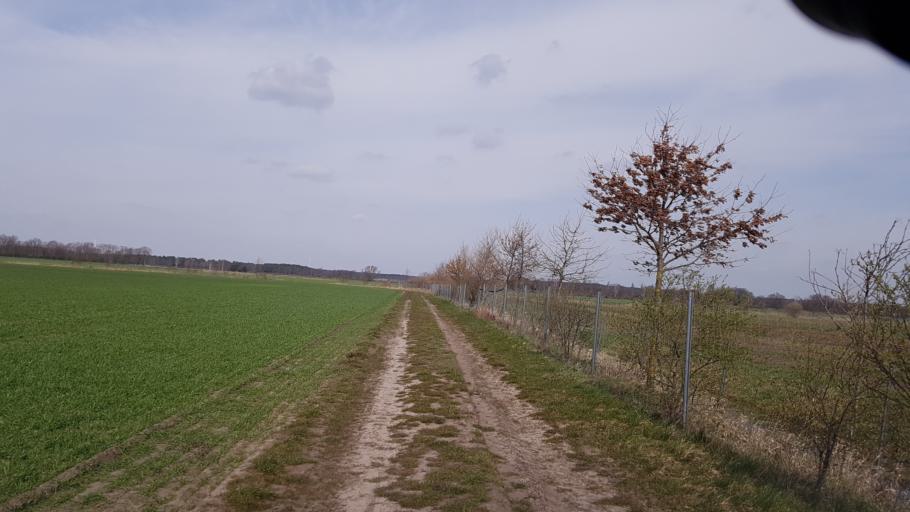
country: DE
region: Brandenburg
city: Bronkow
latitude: 51.6362
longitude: 13.9199
